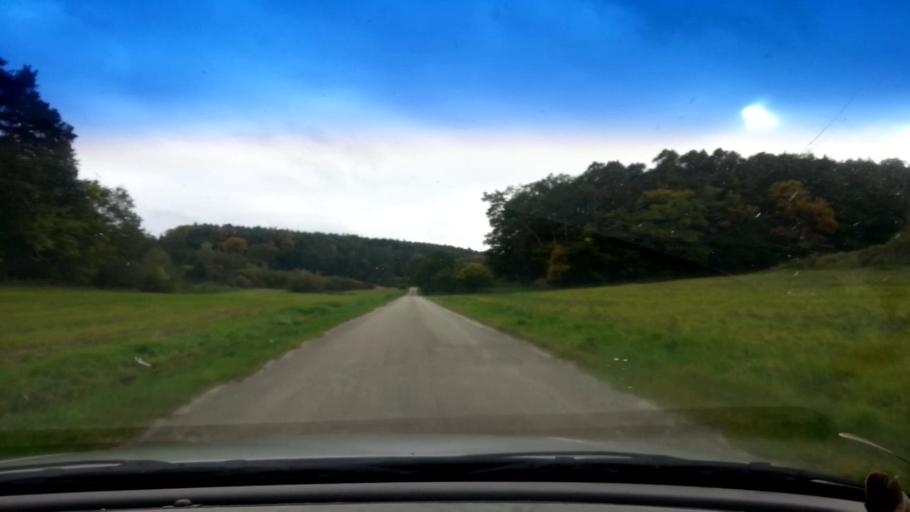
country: DE
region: Bavaria
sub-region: Upper Franconia
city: Priesendorf
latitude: 49.8960
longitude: 10.7093
